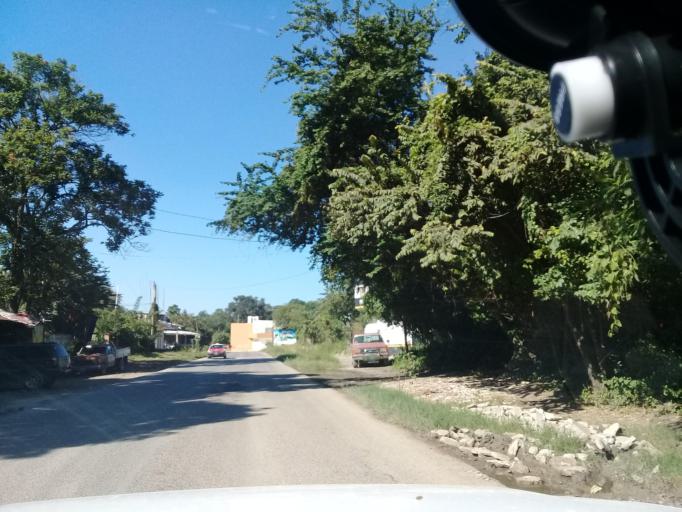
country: MX
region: Hidalgo
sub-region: Huejutla de Reyes
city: Parque de Poblamiento Solidaridad
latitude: 21.1614
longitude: -98.4039
